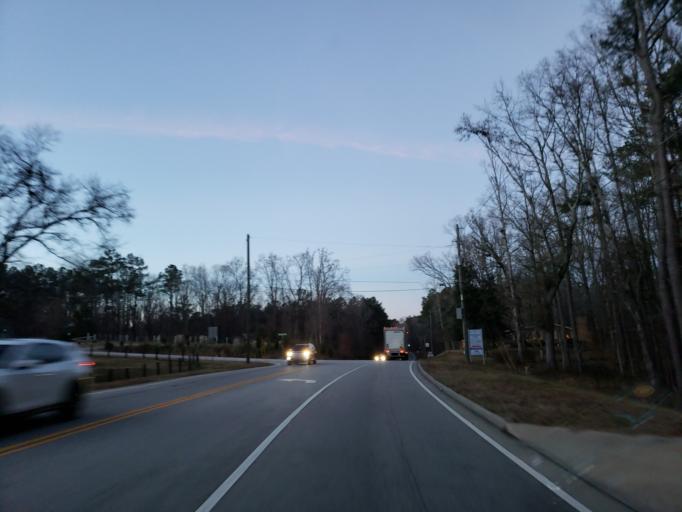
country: US
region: Georgia
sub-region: Paulding County
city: Hiram
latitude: 33.9581
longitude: -84.7079
